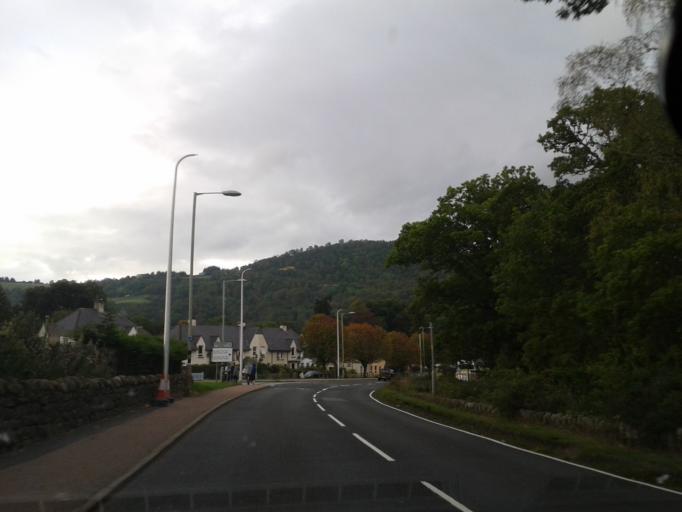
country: GB
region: Scotland
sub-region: Highland
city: Beauly
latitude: 57.3317
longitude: -4.4811
